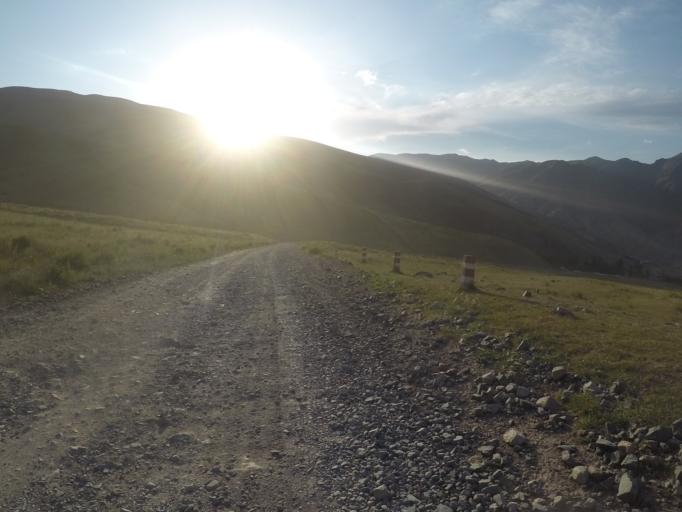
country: KG
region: Chuy
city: Bishkek
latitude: 42.6583
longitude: 74.6529
